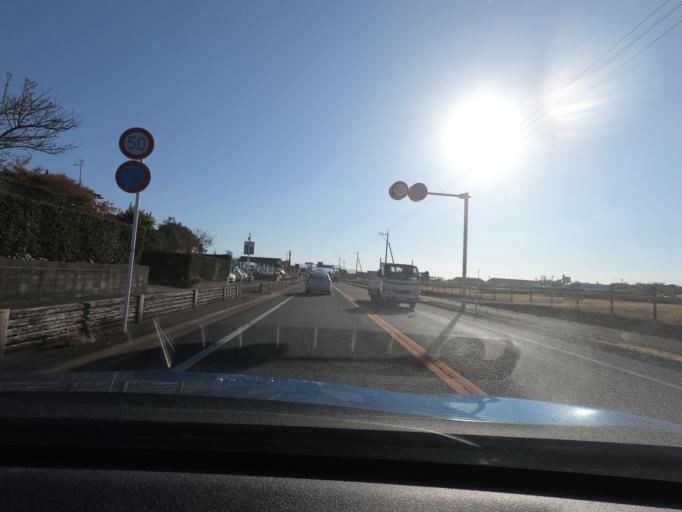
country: JP
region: Kagoshima
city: Izumi
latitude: 32.1279
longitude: 130.3440
